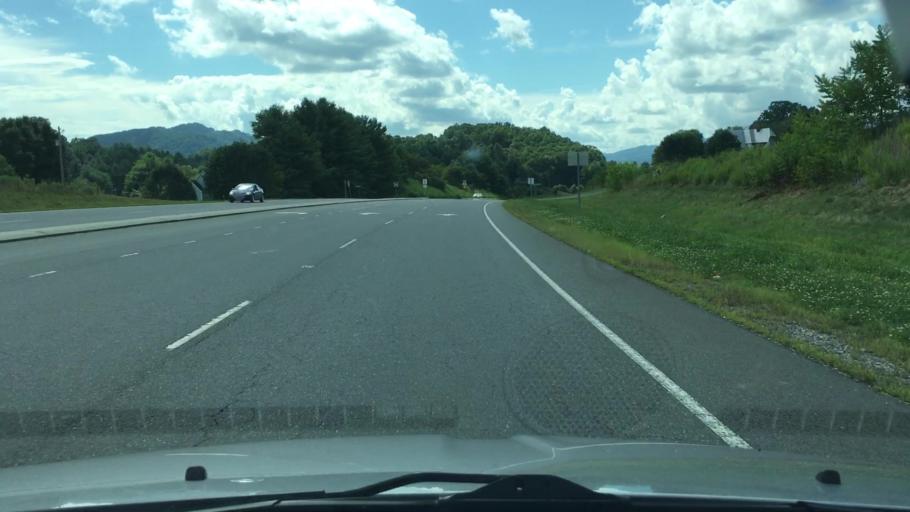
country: US
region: North Carolina
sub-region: Yancey County
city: Burnsville
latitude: 35.9100
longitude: -82.3606
